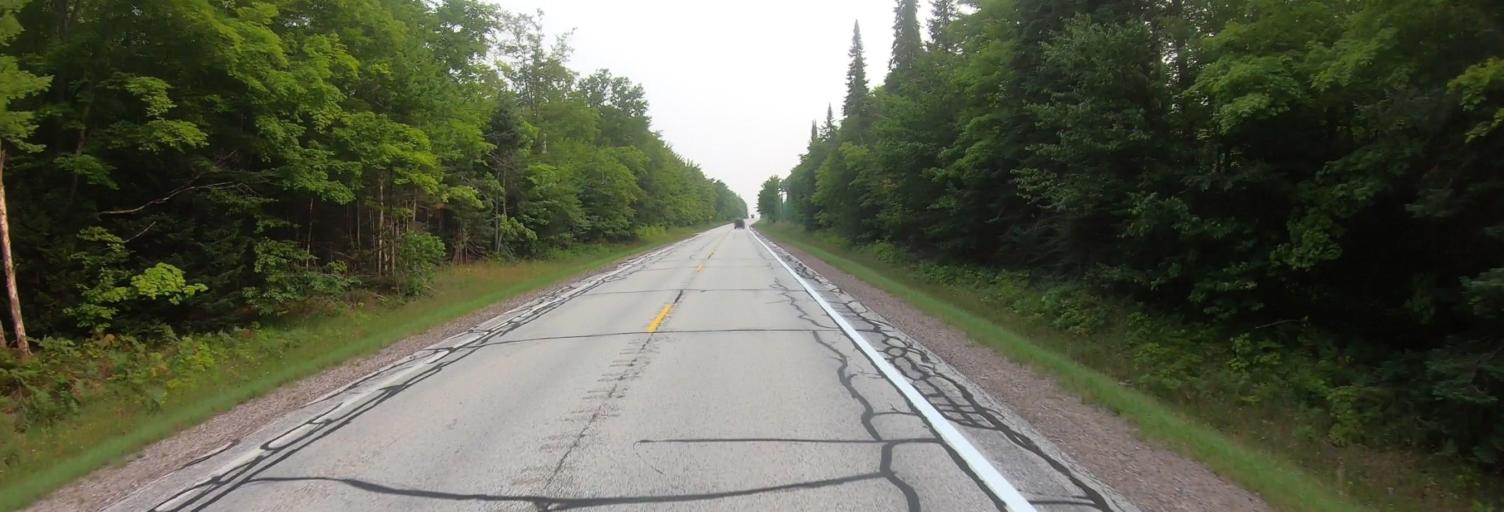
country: US
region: Michigan
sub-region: Luce County
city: Newberry
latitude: 46.4910
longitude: -85.0986
